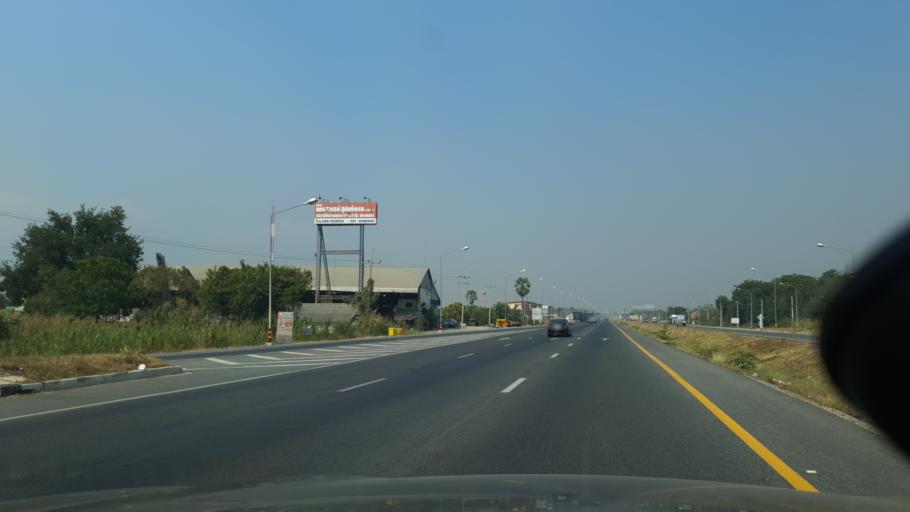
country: TH
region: Nakhon Sawan
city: Nakhon Sawan
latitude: 15.6384
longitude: 100.0952
